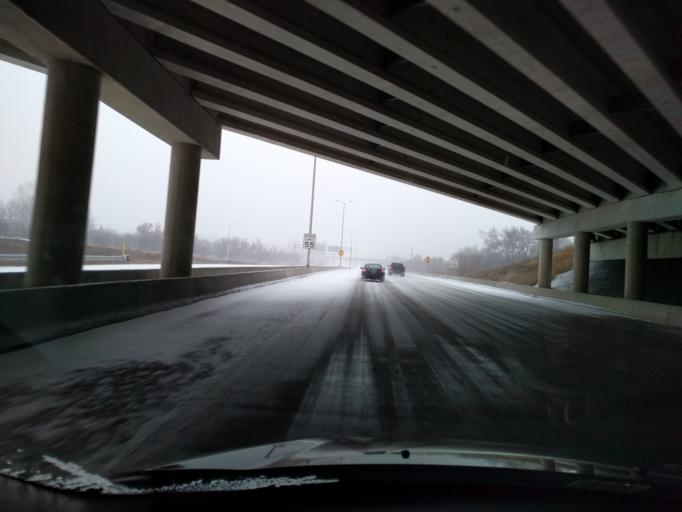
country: US
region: Wisconsin
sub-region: Waukesha County
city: Butler
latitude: 43.1507
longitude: -88.0548
